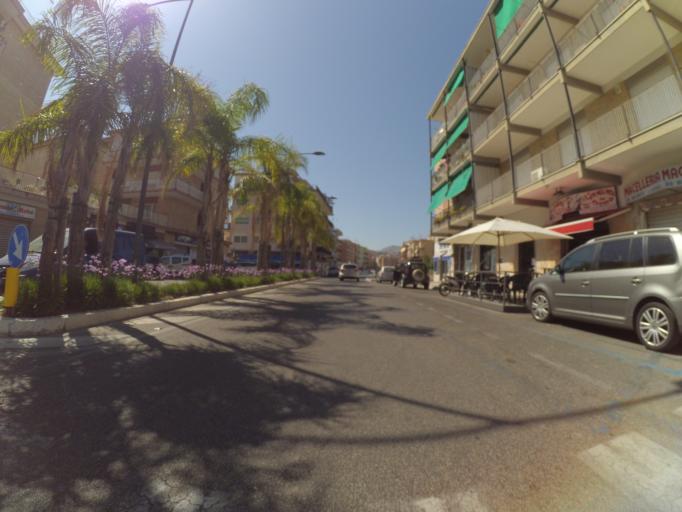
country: IT
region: Latium
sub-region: Provincia di Latina
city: Gaeta
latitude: 41.2134
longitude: 13.5648
